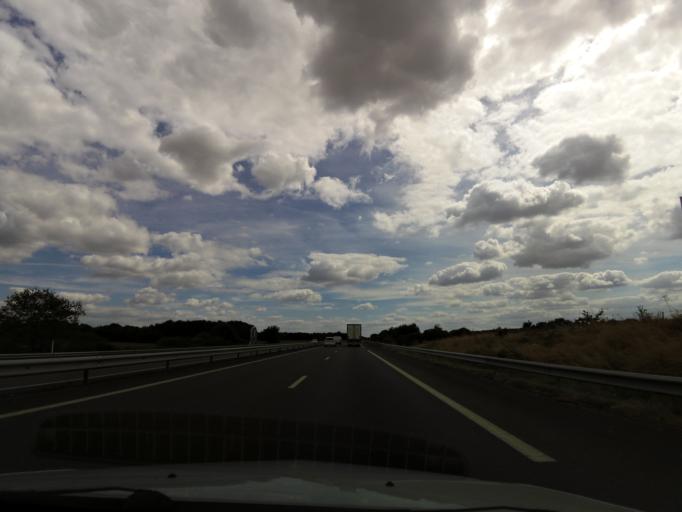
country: FR
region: Pays de la Loire
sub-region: Departement de la Loire-Atlantique
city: La Planche
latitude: 47.0082
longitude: -1.3874
